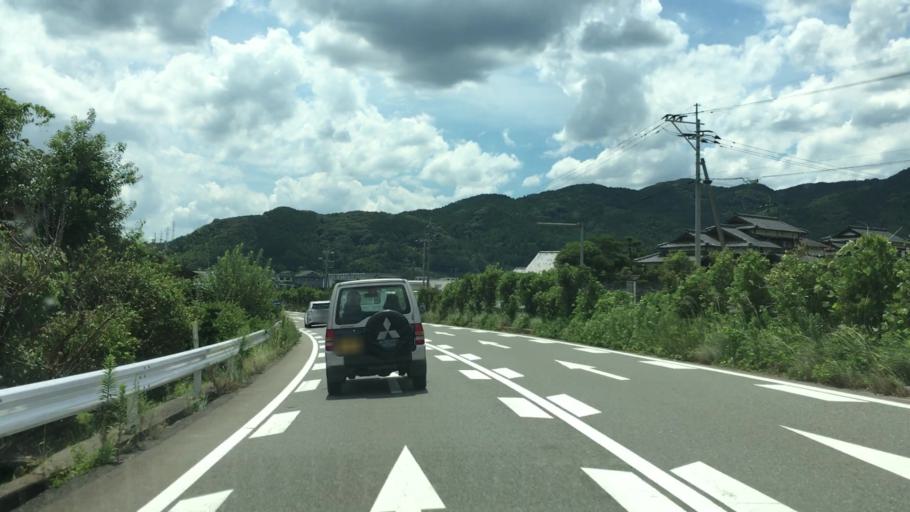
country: JP
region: Saga Prefecture
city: Tosu
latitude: 33.4219
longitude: 130.5120
